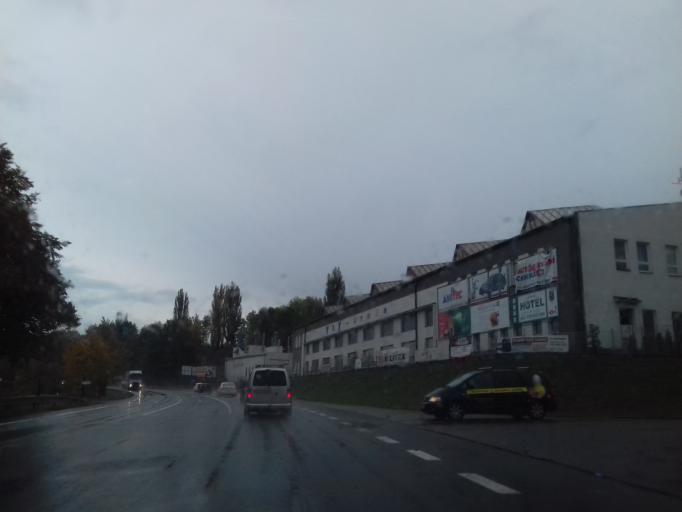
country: CZ
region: Pardubicky
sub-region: Okres Svitavy
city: Litomysl
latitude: 49.8826
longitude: 16.2933
